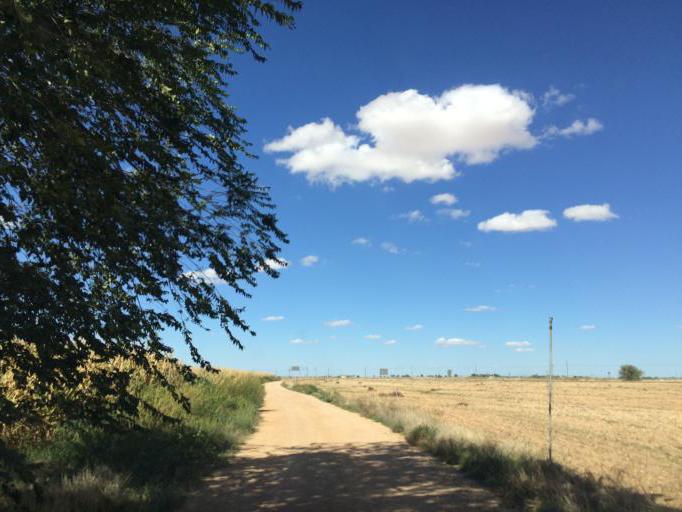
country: ES
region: Castille-La Mancha
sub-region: Provincia de Albacete
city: Albacete
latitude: 38.9416
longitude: -1.8382
